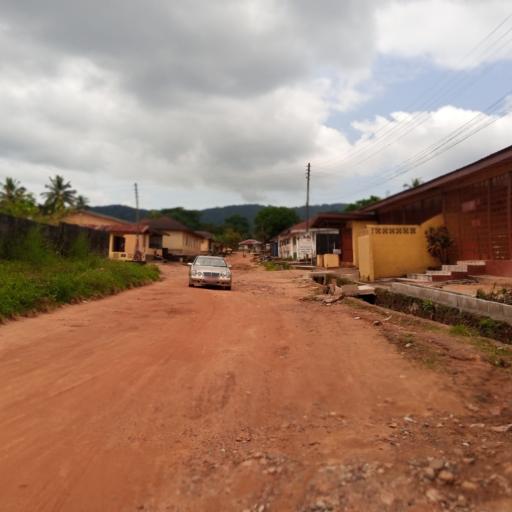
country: SL
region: Eastern Province
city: Kenema
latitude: 7.8885
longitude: -11.1883
